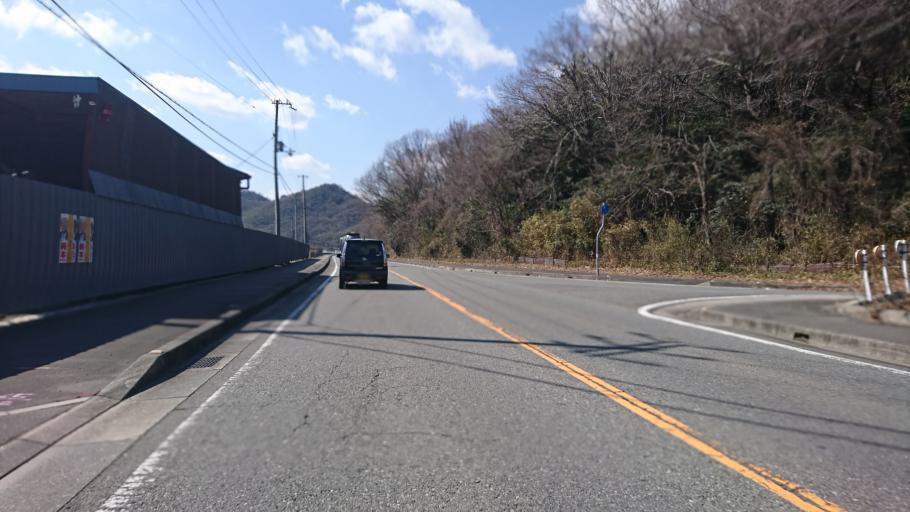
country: JP
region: Hyogo
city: Himeji
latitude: 34.8583
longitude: 134.7835
